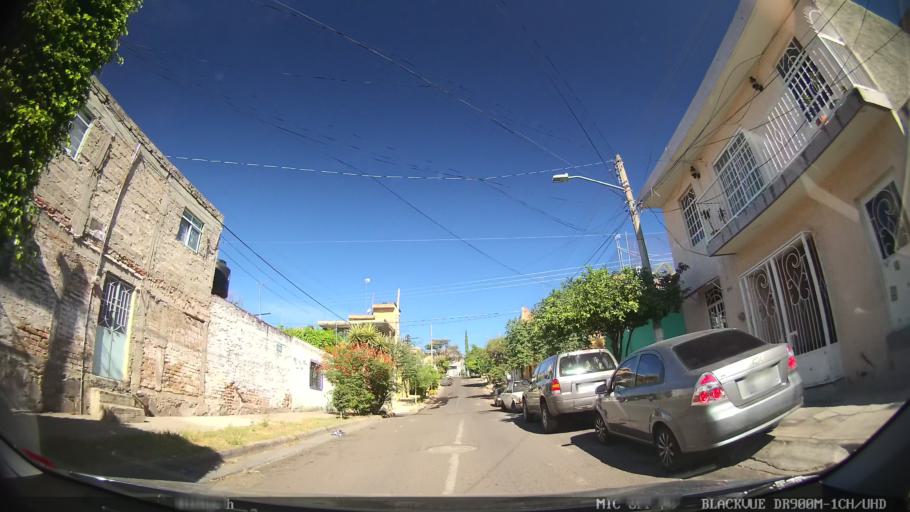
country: MX
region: Jalisco
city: Tlaquepaque
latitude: 20.6903
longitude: -103.2756
